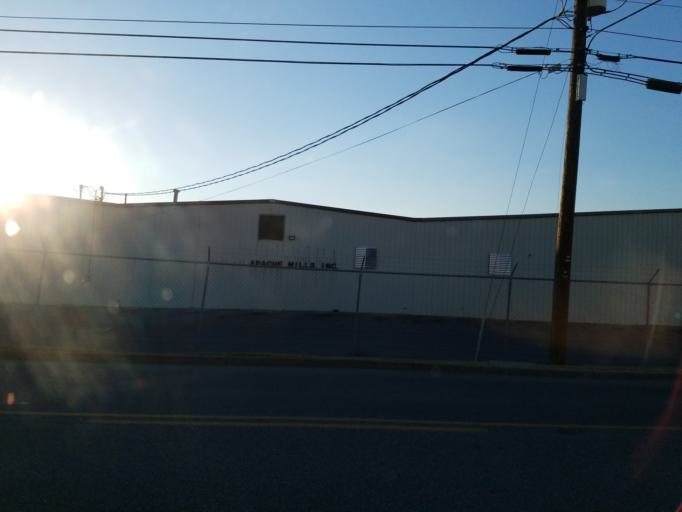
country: US
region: Georgia
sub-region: Gordon County
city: Calhoun
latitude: 34.4927
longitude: -84.9557
